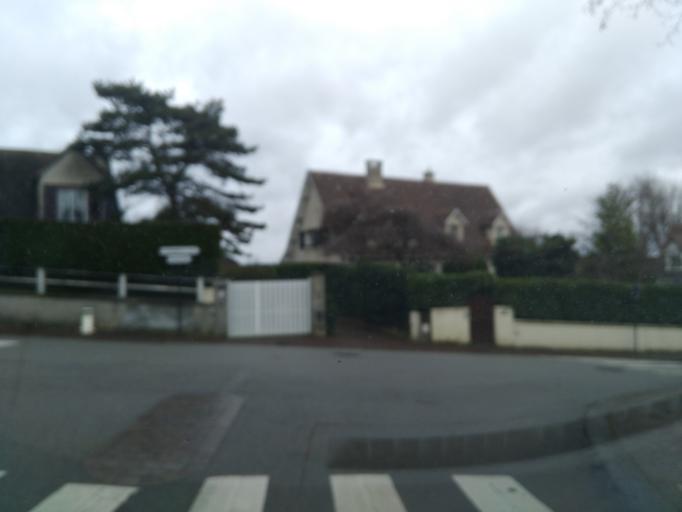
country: FR
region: Ile-de-France
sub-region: Departement des Yvelines
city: Chambourcy
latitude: 48.9074
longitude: 2.0379
